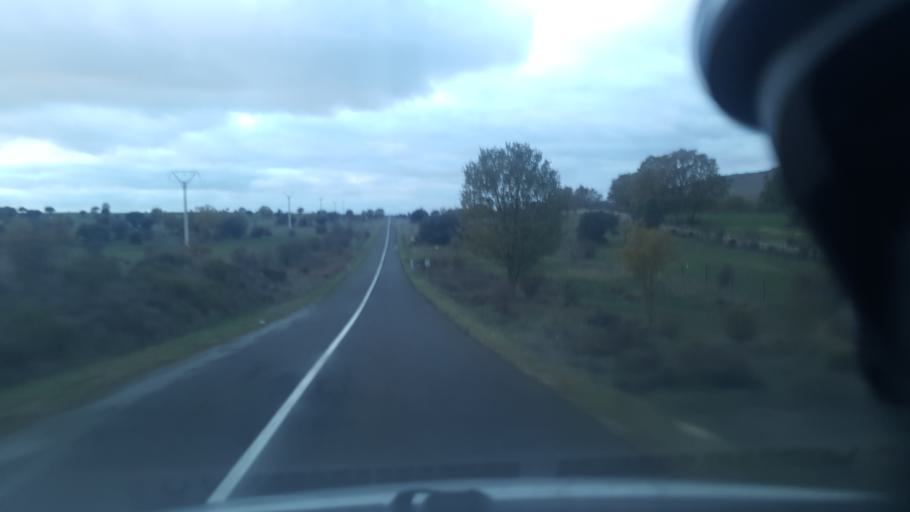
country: ES
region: Castille and Leon
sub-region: Provincia de Avila
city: Las Navas del Marques
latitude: 40.7054
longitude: -4.3391
